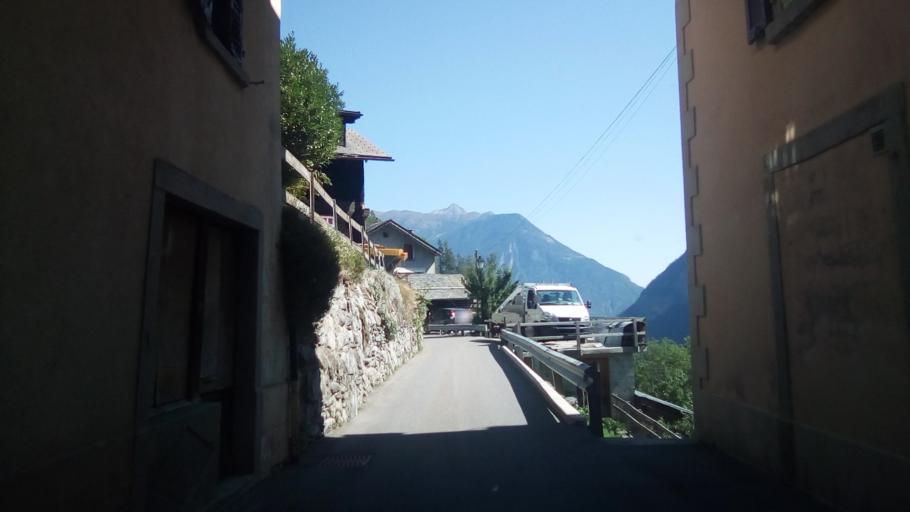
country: CH
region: Valais
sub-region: Saint-Maurice District
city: Salvan
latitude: 46.1021
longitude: 6.9989
